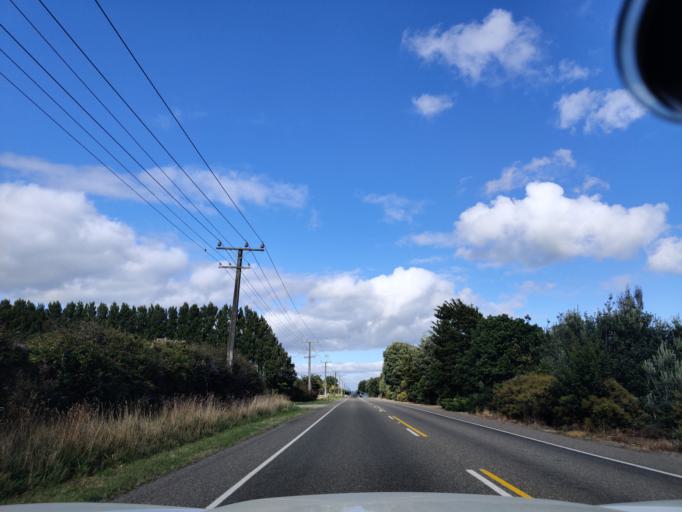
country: NZ
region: Manawatu-Wanganui
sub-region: Horowhenua District
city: Levin
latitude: -40.6350
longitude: 175.3017
